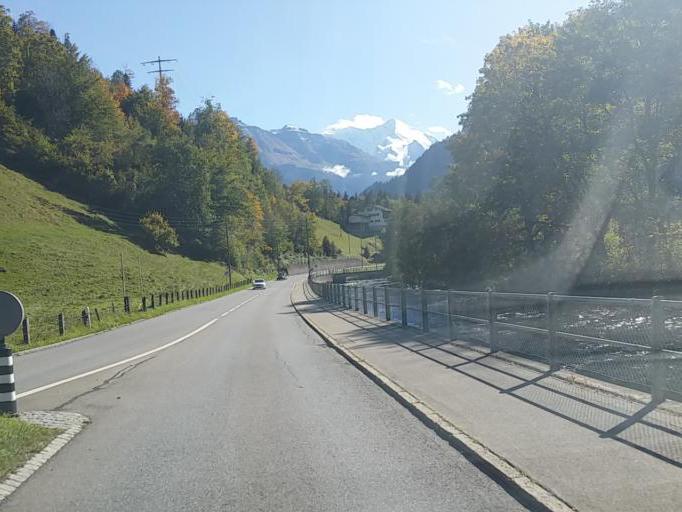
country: CH
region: Bern
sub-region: Frutigen-Niedersimmental District
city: Frutigen
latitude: 46.5558
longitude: 7.6612
